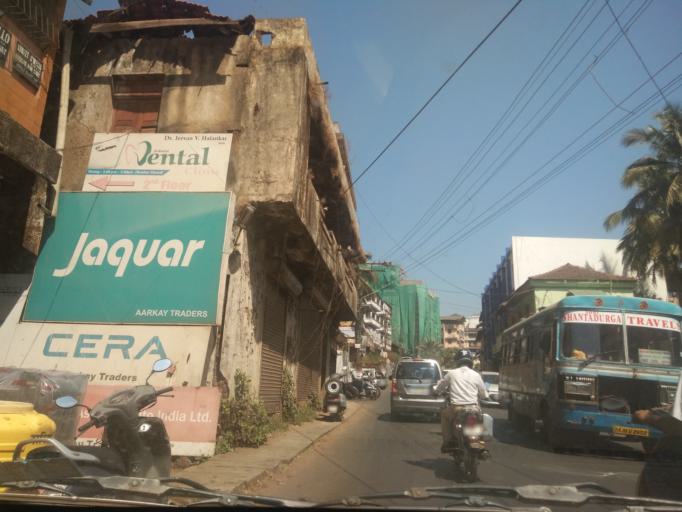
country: IN
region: Goa
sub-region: North Goa
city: Mapuca
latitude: 15.5913
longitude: 73.8128
